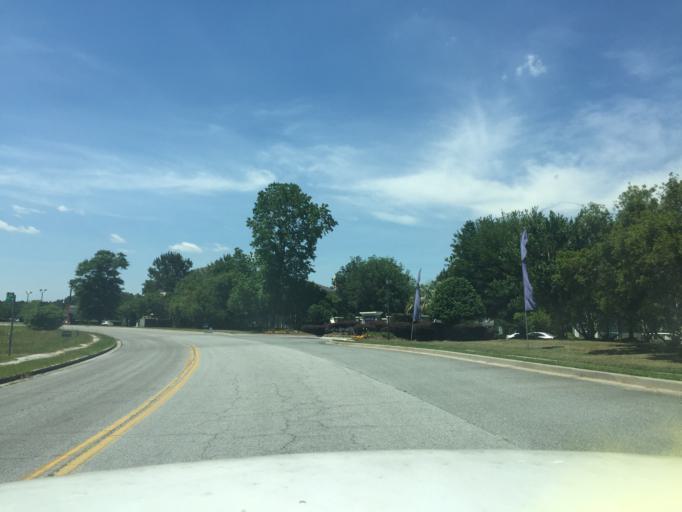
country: US
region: Georgia
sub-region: Chatham County
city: Georgetown
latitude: 32.0067
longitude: -81.2748
